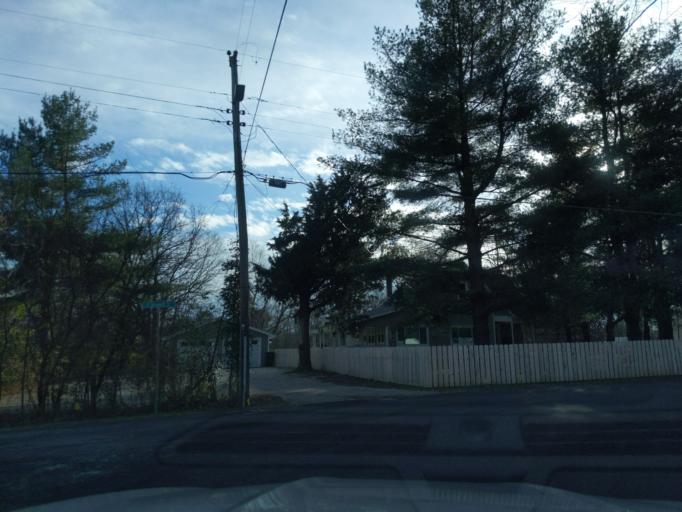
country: US
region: Indiana
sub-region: Decatur County
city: Westport
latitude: 39.1779
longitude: -85.5688
